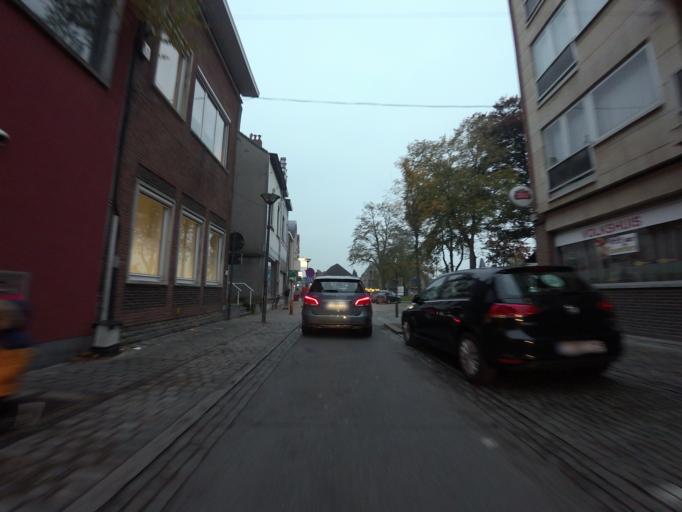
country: BE
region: Flanders
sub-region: Provincie Vlaams-Brabant
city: Zaventem
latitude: 50.8837
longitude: 4.4714
